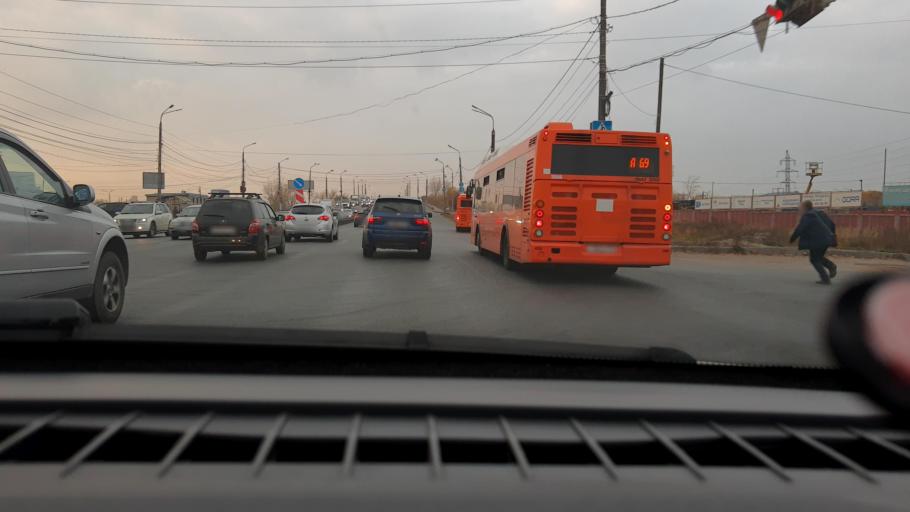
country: RU
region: Nizjnij Novgorod
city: Nizhniy Novgorod
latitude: 56.2950
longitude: 43.8849
